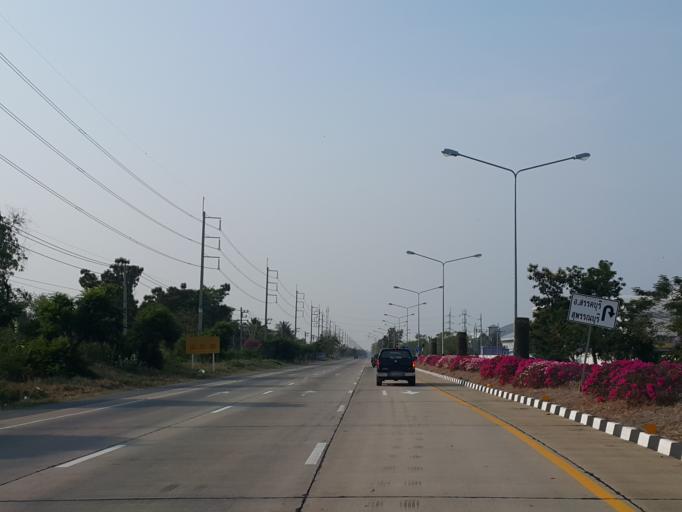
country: TH
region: Chai Nat
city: Hankha
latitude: 14.9526
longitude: 100.0812
